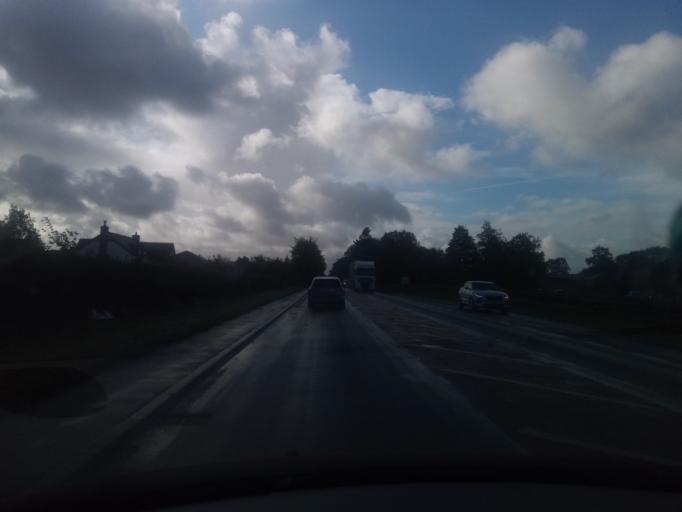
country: GB
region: England
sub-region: Cumbria
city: Carlisle
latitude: 54.9397
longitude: -2.9444
